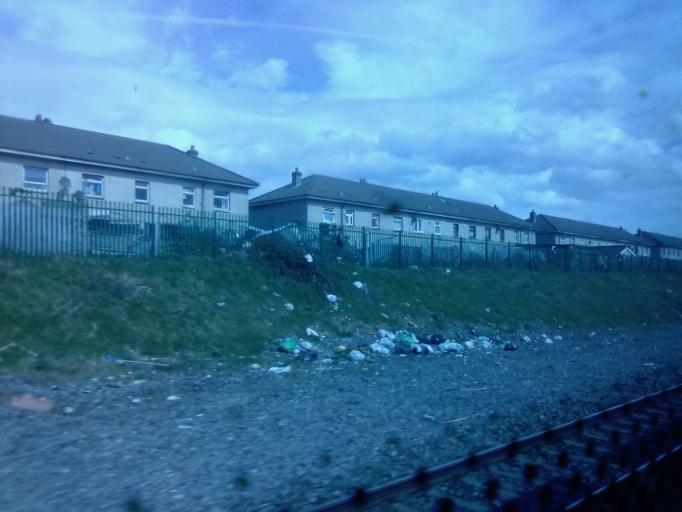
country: IE
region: Leinster
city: Ballyfermot
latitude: 53.3357
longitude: -6.3571
